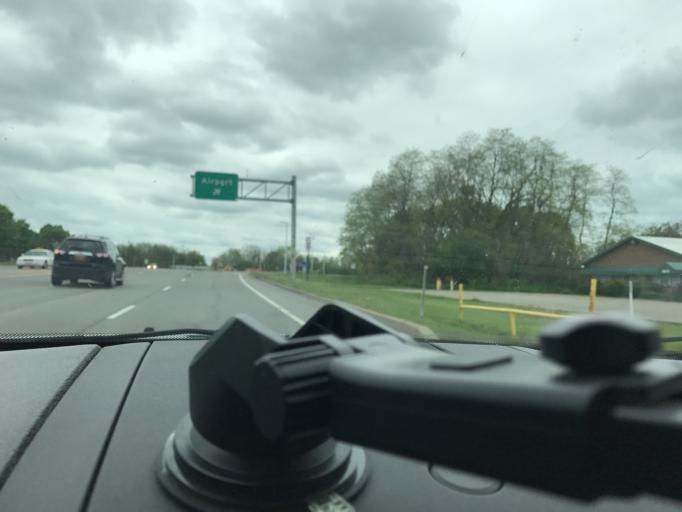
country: US
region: New York
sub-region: Monroe County
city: North Gates
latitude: 43.1308
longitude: -77.6686
